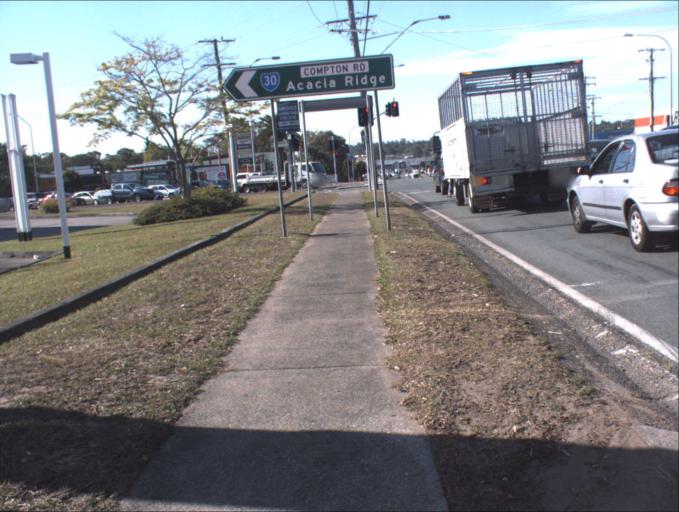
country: AU
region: Queensland
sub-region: Logan
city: Springwood
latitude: -27.6209
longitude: 153.1156
